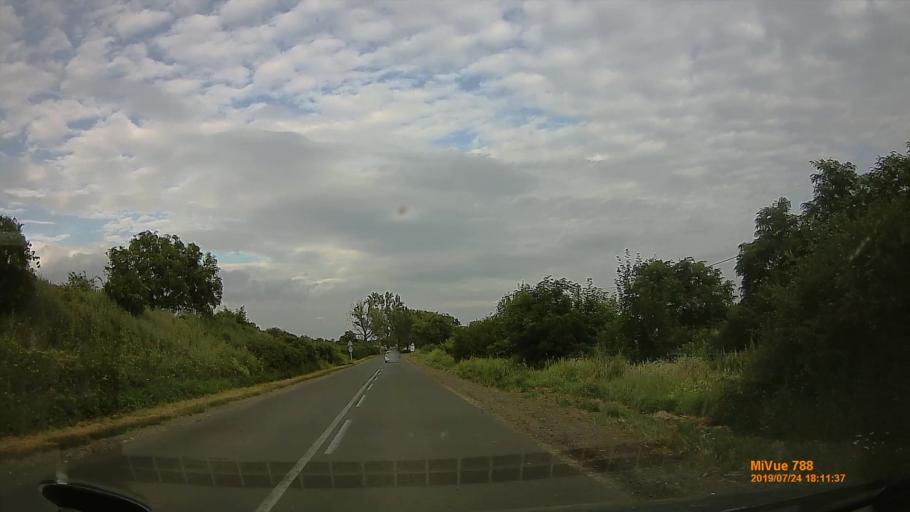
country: HU
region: Borsod-Abauj-Zemplen
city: Tallya
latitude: 48.2445
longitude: 21.2015
